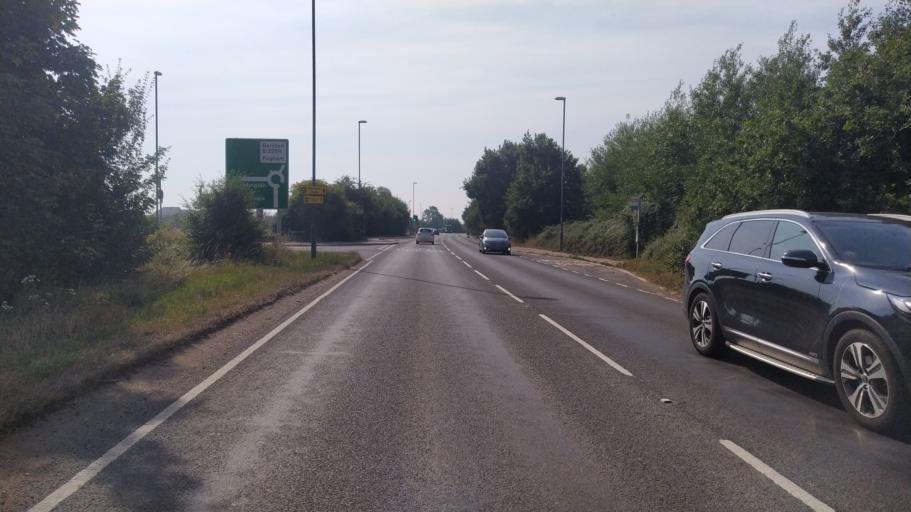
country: GB
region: England
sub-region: West Sussex
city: Bognor Regis
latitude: 50.8076
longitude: -0.7020
